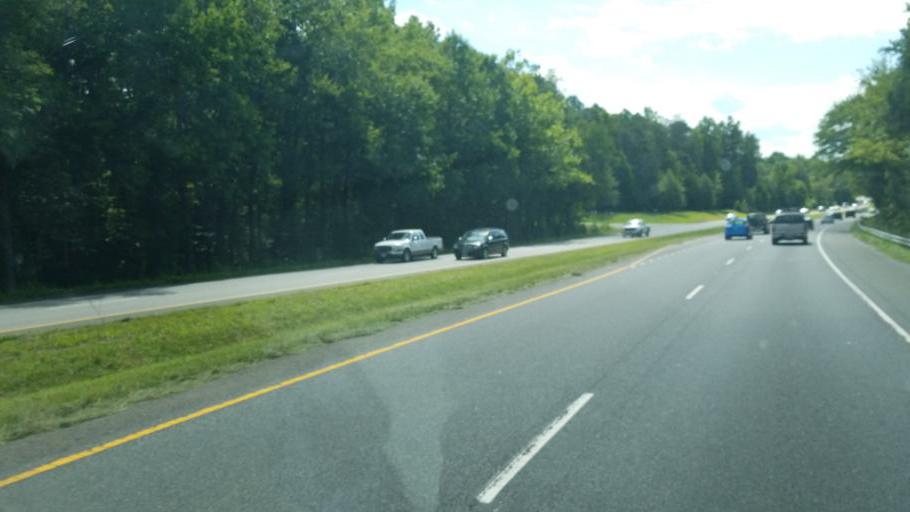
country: US
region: Virginia
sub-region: Stafford County
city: Falmouth
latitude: 38.4158
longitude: -77.6087
